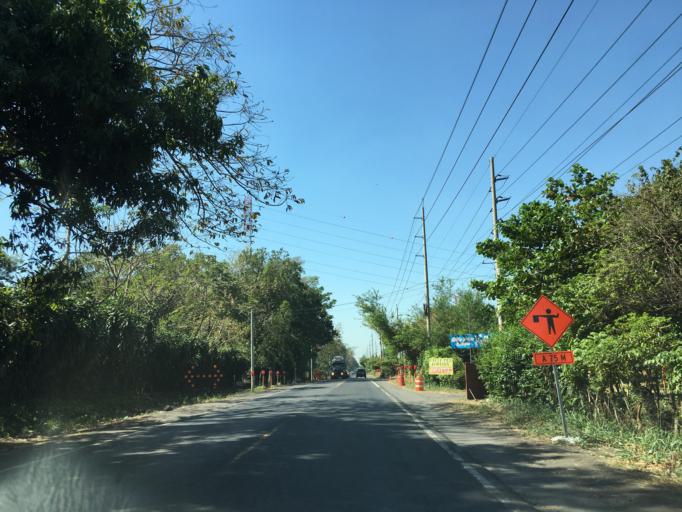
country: GT
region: Escuintla
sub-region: Municipio de Masagua
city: Masagua
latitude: 14.2285
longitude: -90.8258
